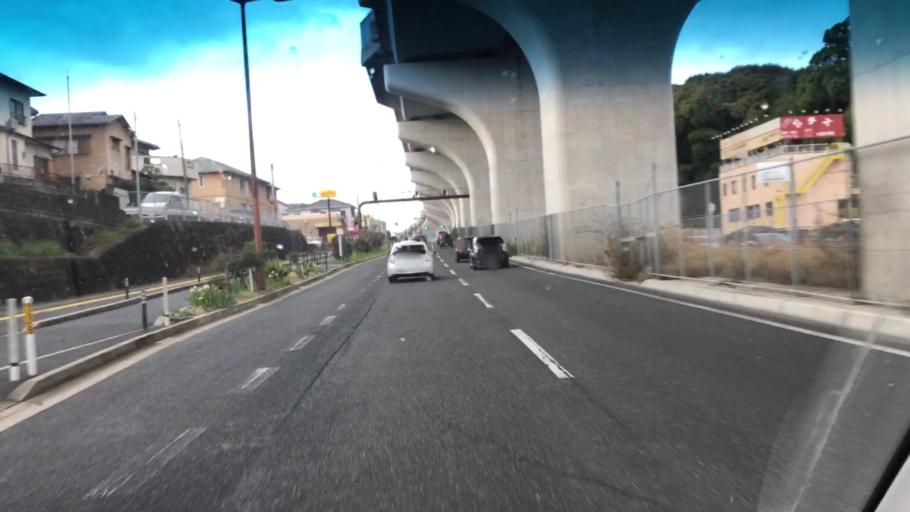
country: JP
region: Fukuoka
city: Maebaru-chuo
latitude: 33.5686
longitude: 130.3061
